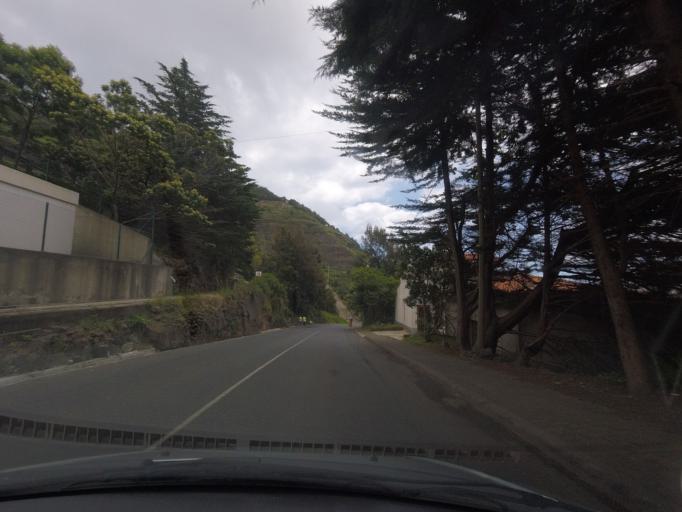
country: PT
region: Madeira
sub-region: Machico
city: Canical
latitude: 32.7370
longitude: -16.7575
